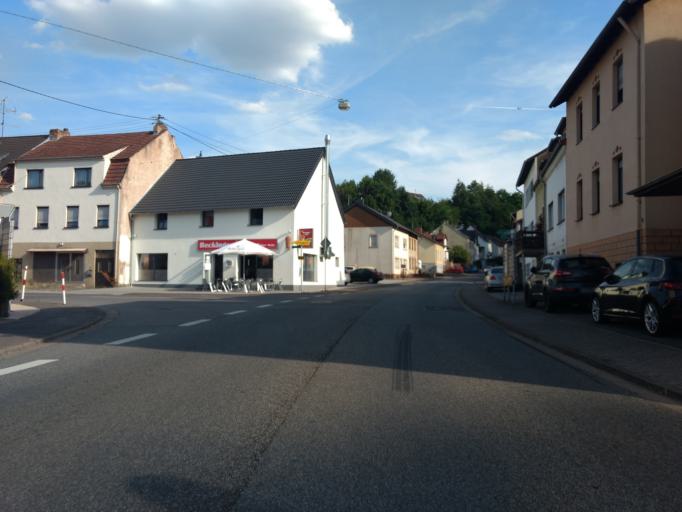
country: DE
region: Saarland
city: Beckingen
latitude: 49.3921
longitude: 6.7021
